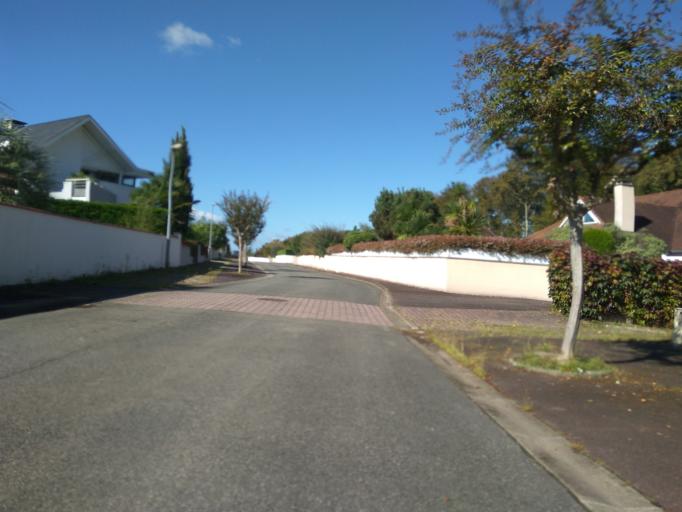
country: FR
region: Aquitaine
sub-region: Departement des Pyrenees-Atlantiques
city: Idron
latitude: 43.2944
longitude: -0.3151
